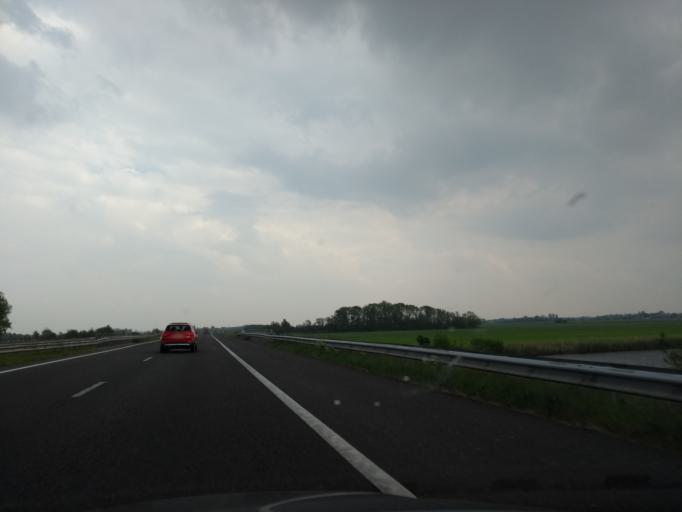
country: NL
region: Friesland
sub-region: Sudwest Fryslan
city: Oppenhuizen
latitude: 52.9832
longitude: 5.7363
